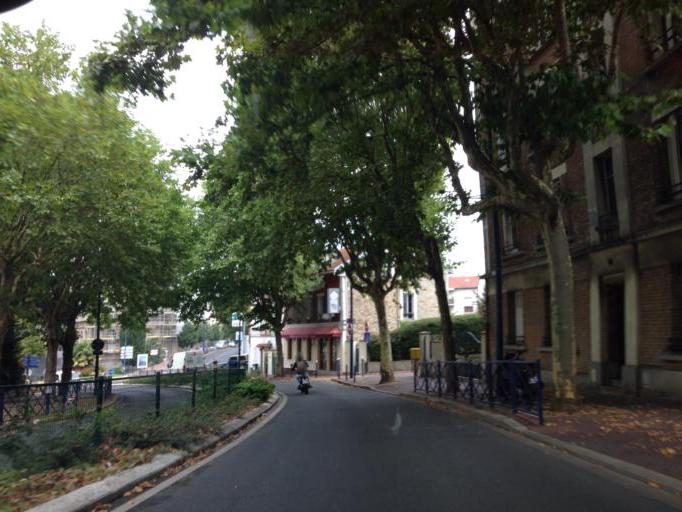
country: FR
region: Ile-de-France
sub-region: Departement des Hauts-de-Seine
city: Clamart
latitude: 48.7984
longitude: 2.2679
